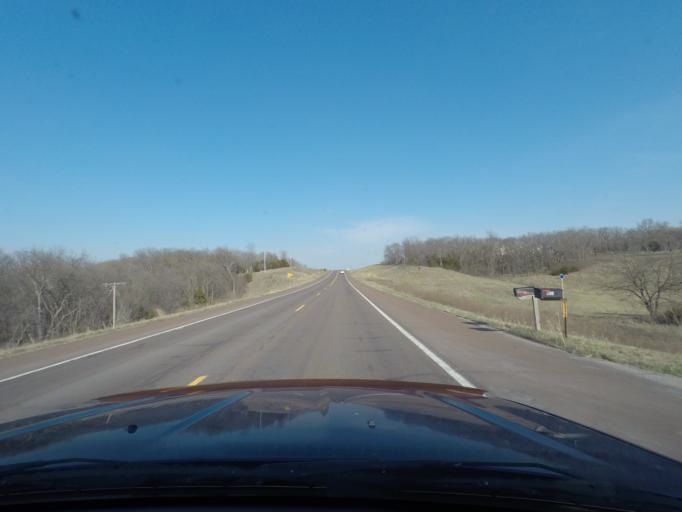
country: US
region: Kansas
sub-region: Douglas County
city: Lawrence
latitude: 39.0004
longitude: -95.3591
